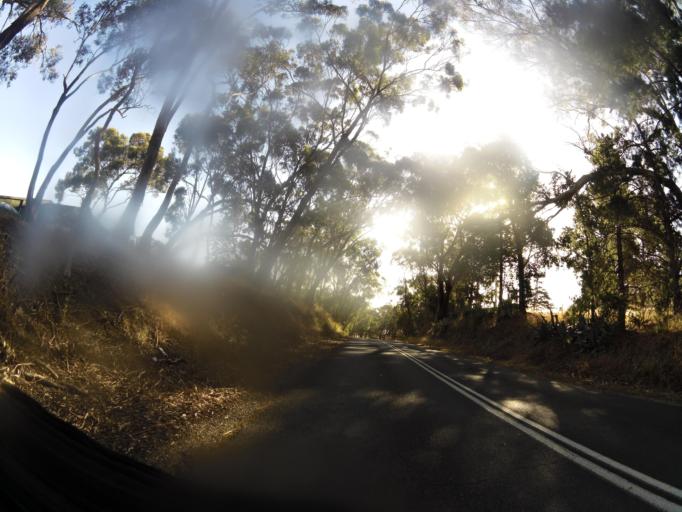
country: AU
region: Victoria
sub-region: Murrindindi
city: Kinglake West
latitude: -37.0213
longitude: 145.1055
